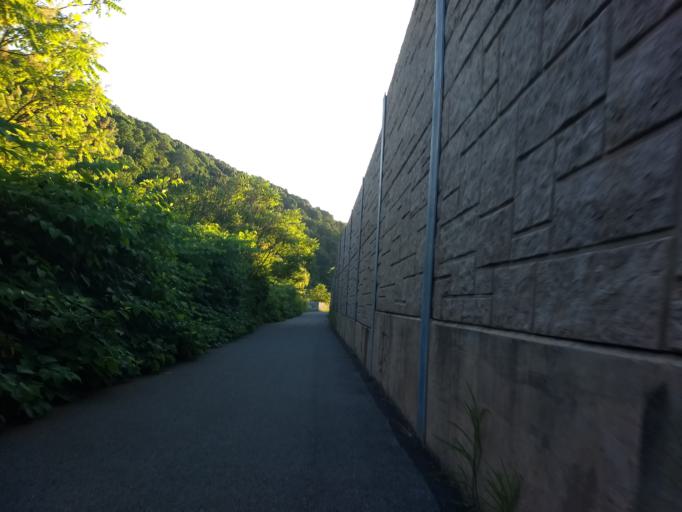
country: US
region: Pennsylvania
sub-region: Allegheny County
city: West Homestead
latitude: 40.3947
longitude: -79.9375
